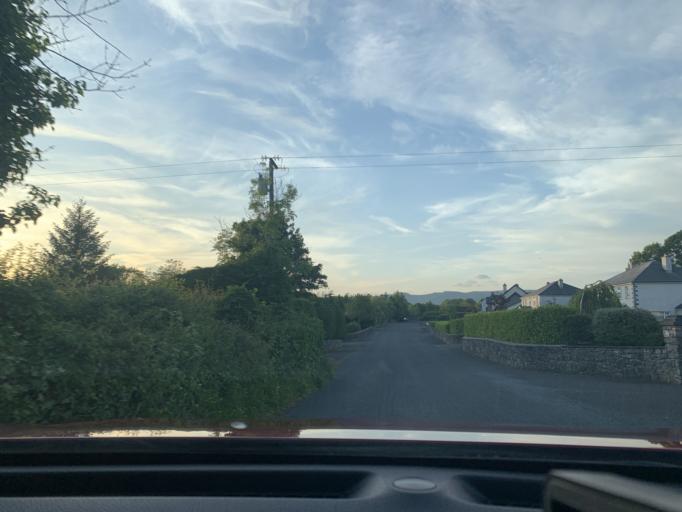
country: IE
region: Connaught
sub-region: Sligo
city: Sligo
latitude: 54.2813
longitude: -8.4327
